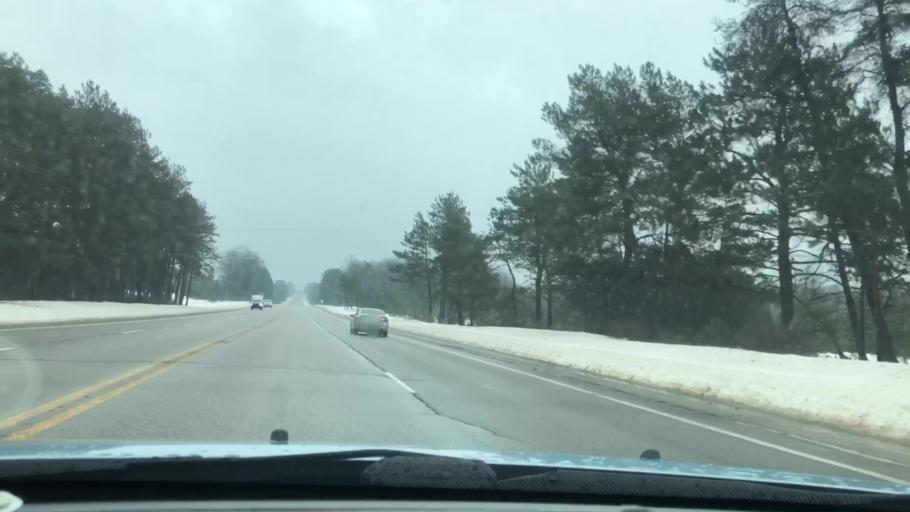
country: US
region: Michigan
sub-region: Otsego County
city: Gaylord
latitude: 45.0621
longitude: -84.8321
